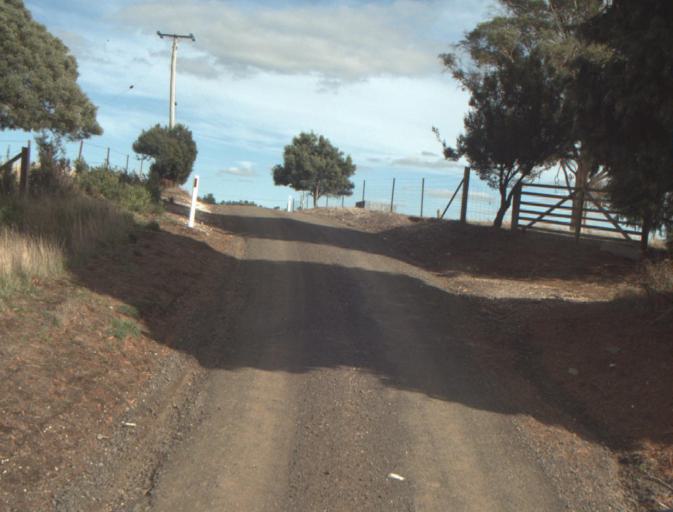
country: AU
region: Tasmania
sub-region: Launceston
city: Mayfield
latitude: -41.1881
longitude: 147.1908
